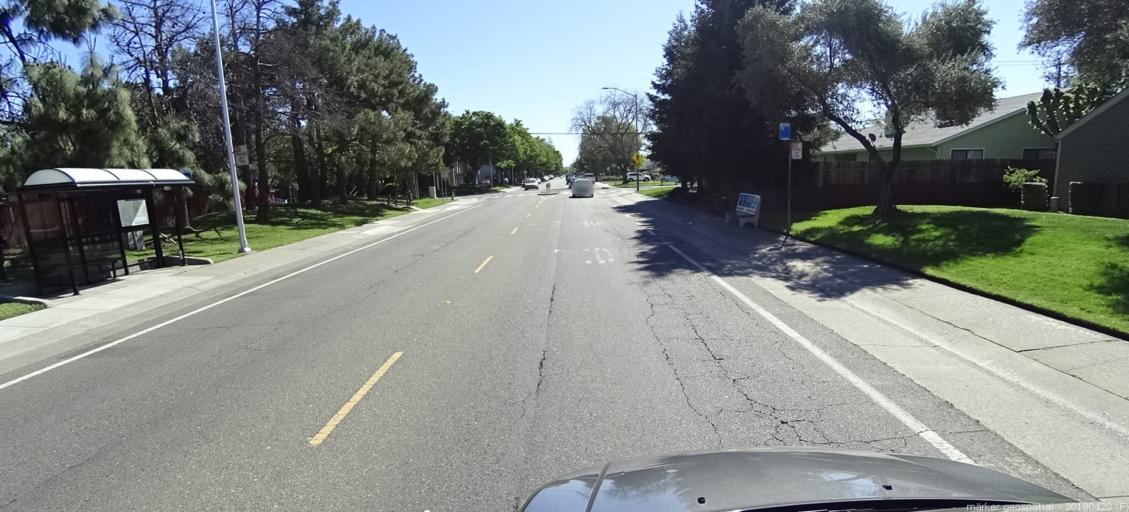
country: US
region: California
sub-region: Sacramento County
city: Parkway
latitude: 38.5467
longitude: -121.4447
